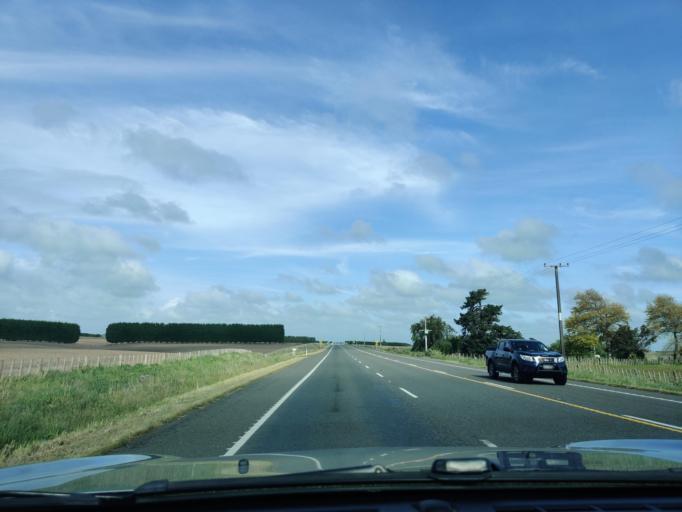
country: NZ
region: Manawatu-Wanganui
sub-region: Wanganui District
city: Wanganui
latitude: -39.9839
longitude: 175.1525
